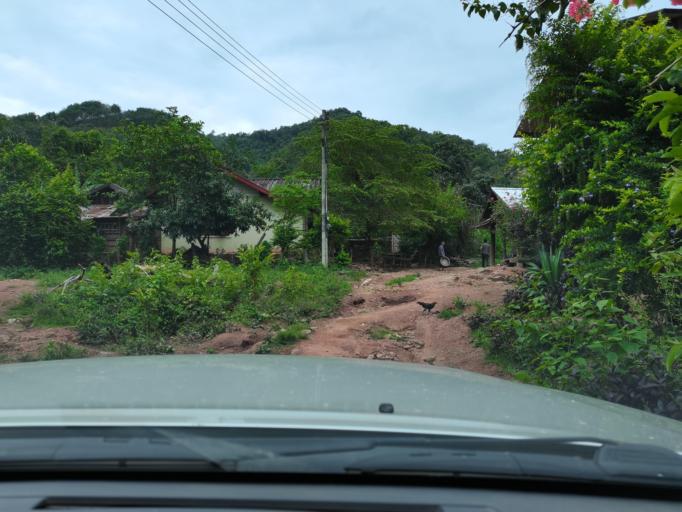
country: LA
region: Loungnamtha
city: Muang Nale
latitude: 20.5032
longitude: 101.0869
